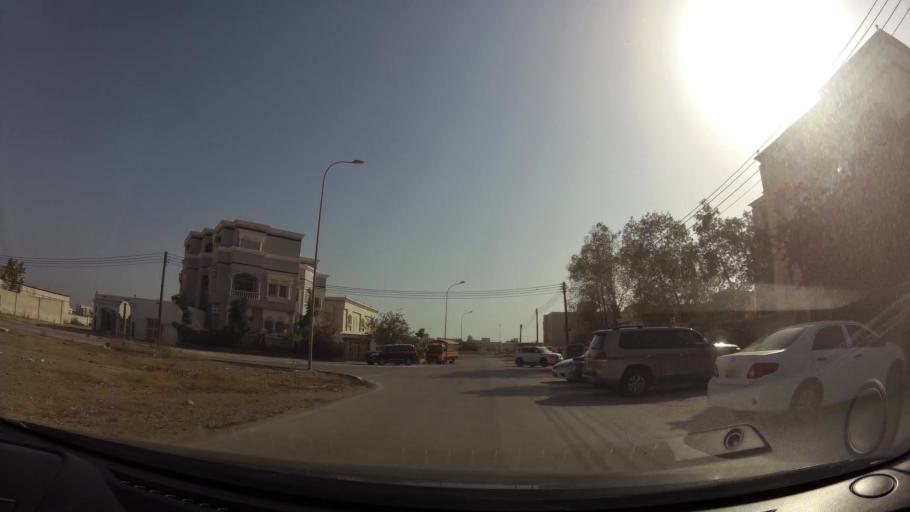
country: OM
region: Zufar
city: Salalah
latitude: 17.0089
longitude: 54.0157
